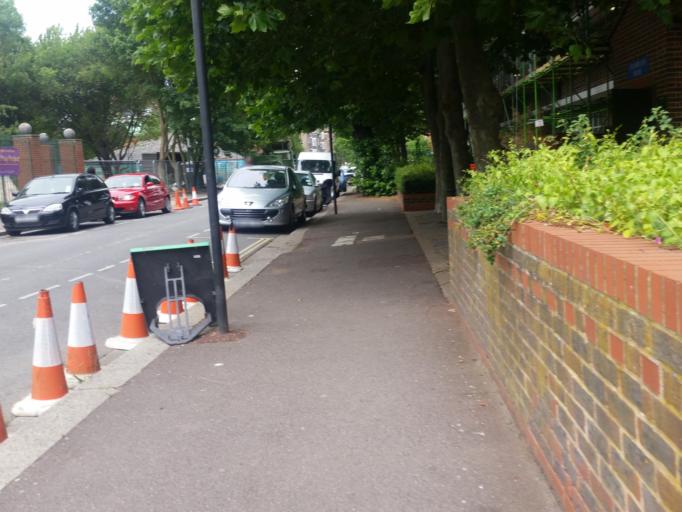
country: GB
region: England
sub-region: Greater London
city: Hammersmith
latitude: 51.5114
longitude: -0.2313
